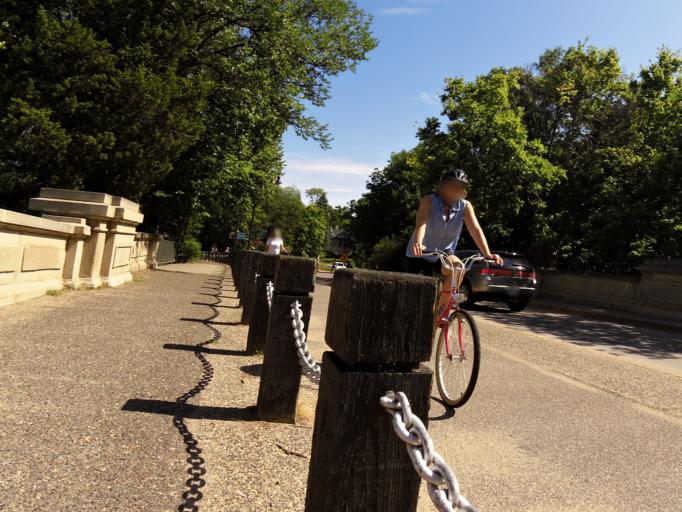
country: US
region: Minnesota
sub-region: Hennepin County
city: Saint Louis Park
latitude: 44.9512
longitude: -93.3061
